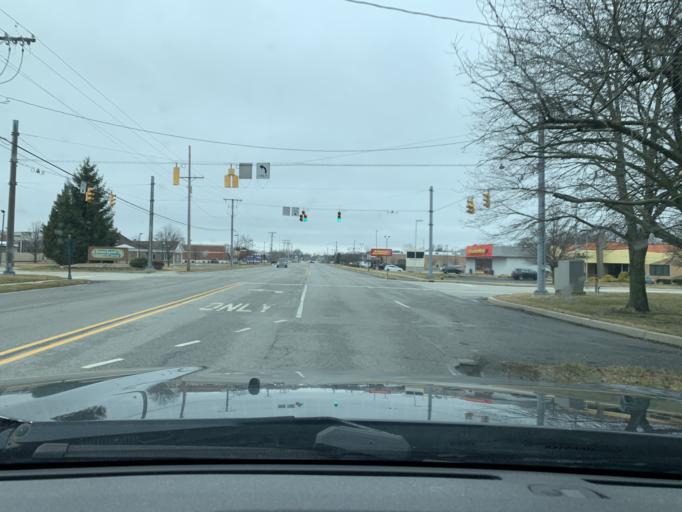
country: US
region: Indiana
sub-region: Porter County
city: Chesterton
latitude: 41.6170
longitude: -87.0344
